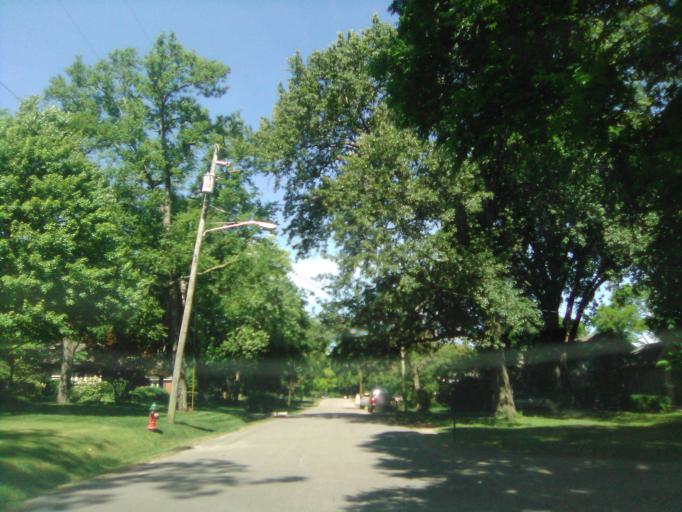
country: US
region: Tennessee
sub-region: Davidson County
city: Belle Meade
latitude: 36.1258
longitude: -86.8348
